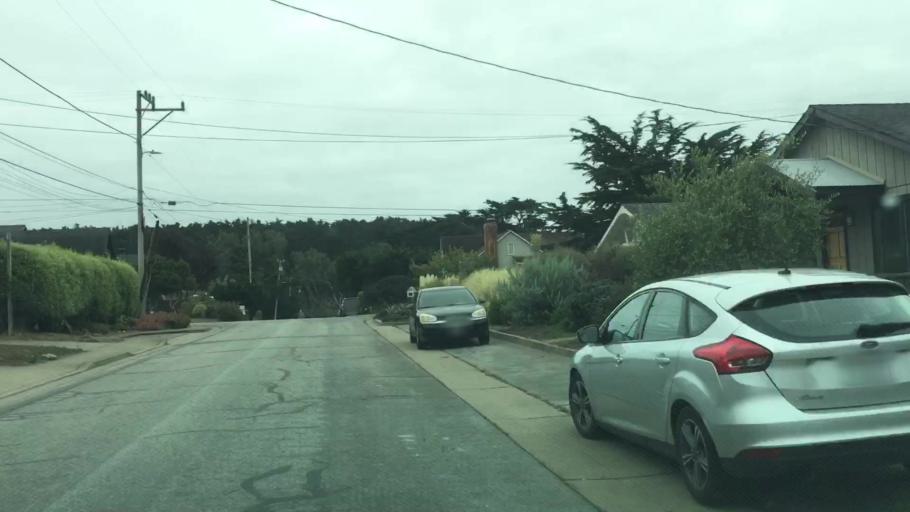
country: US
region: California
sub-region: San Mateo County
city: Moss Beach
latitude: 37.5255
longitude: -122.5138
